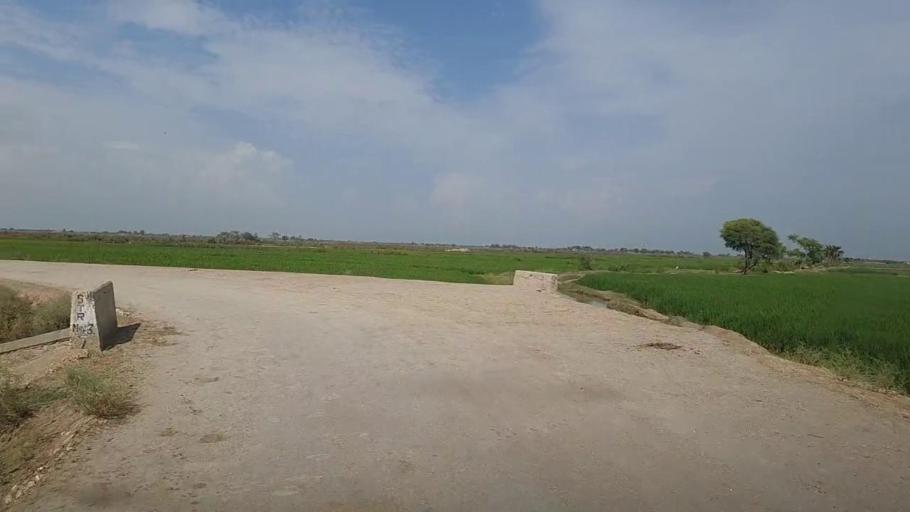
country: PK
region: Sindh
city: Thul
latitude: 28.2744
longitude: 68.8224
